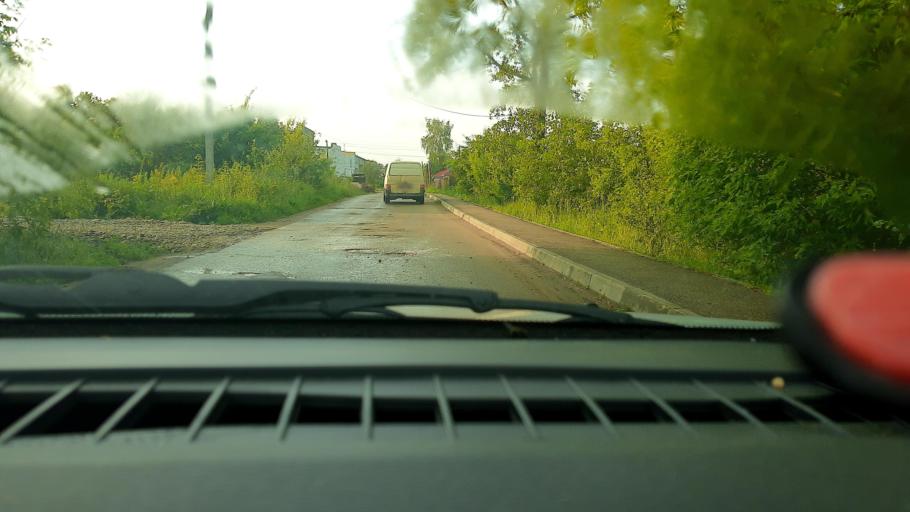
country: RU
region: Nizjnij Novgorod
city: Lukoyanov
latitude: 55.0425
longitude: 44.4938
